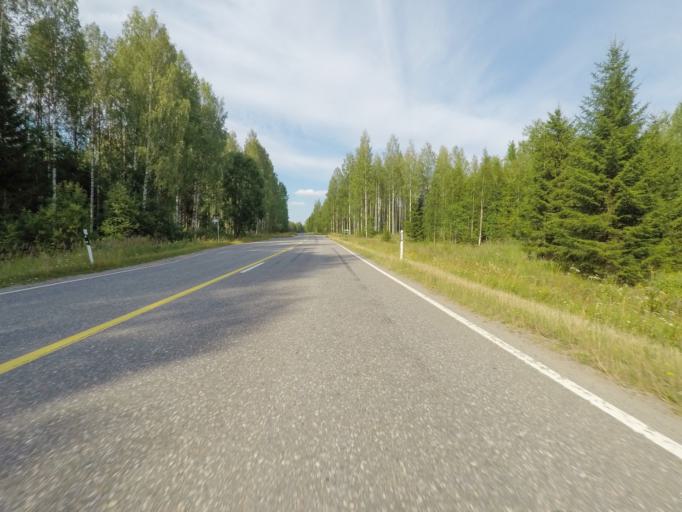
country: FI
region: Southern Savonia
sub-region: Savonlinna
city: Sulkava
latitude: 61.8363
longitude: 28.4609
